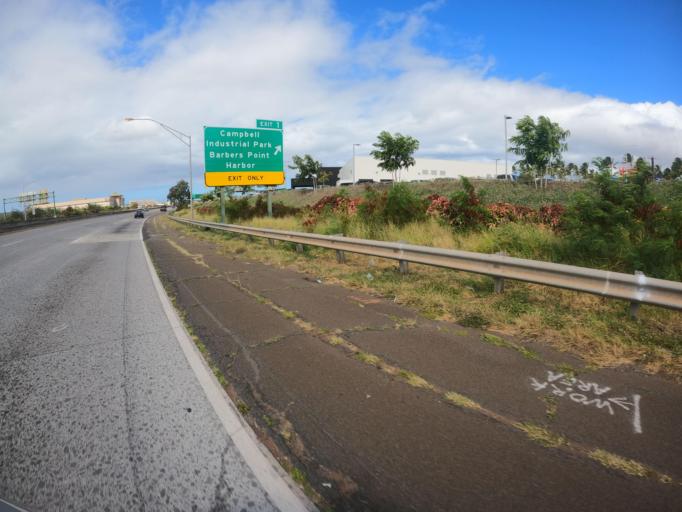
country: US
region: Hawaii
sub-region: Honolulu County
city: Makakilo City
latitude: 21.3341
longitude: -158.0856
